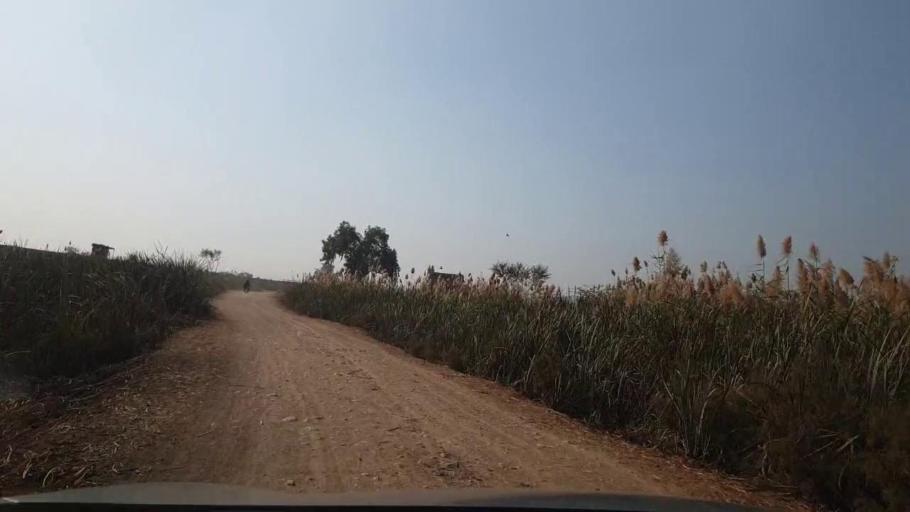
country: PK
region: Sindh
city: Mirpur Khas
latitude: 25.6427
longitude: 68.9106
